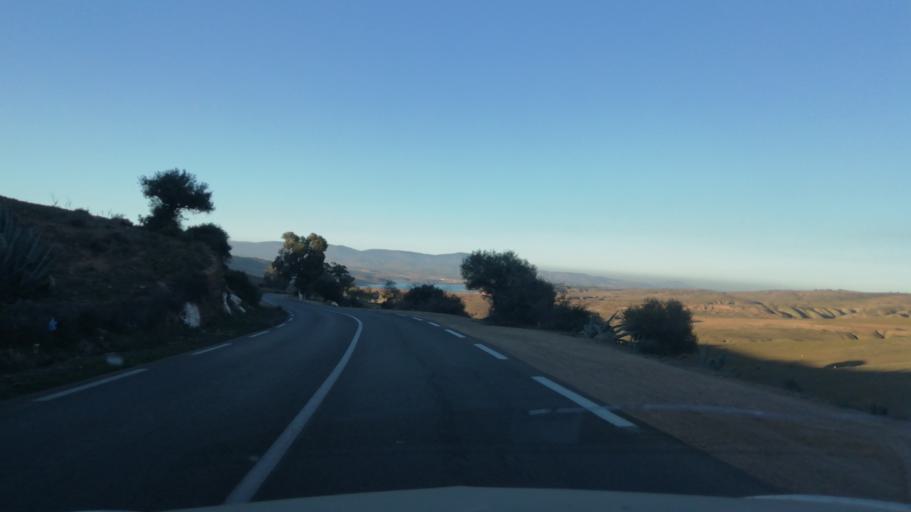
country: DZ
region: Tlemcen
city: Beni Mester
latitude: 34.8230
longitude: -1.6375
